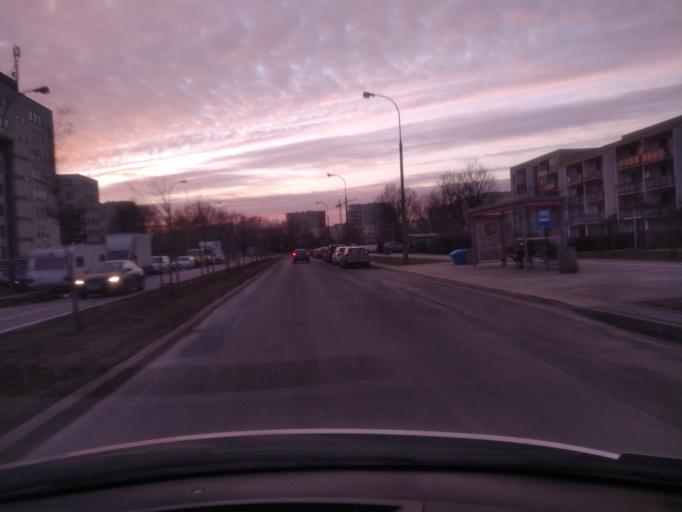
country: PL
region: Masovian Voivodeship
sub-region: Warszawa
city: Praga Poludnie
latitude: 52.2227
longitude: 21.0872
